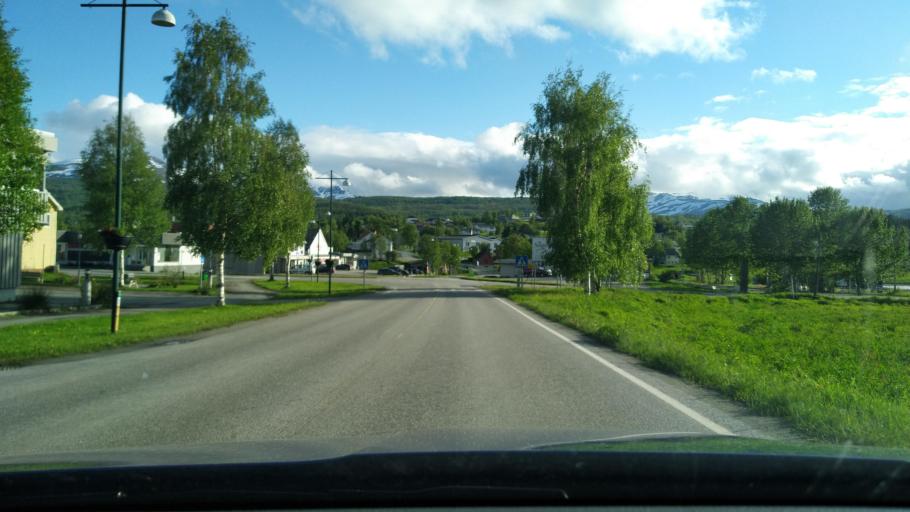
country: NO
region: Troms
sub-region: Sorreisa
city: Sorreisa
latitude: 69.1459
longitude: 18.1544
